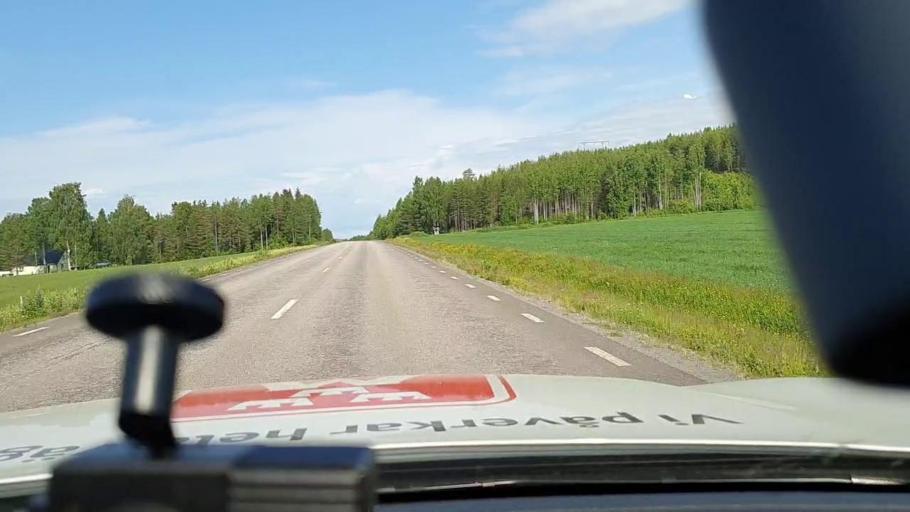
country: SE
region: Norrbotten
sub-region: Bodens Kommun
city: Boden
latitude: 65.9142
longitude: 21.3407
